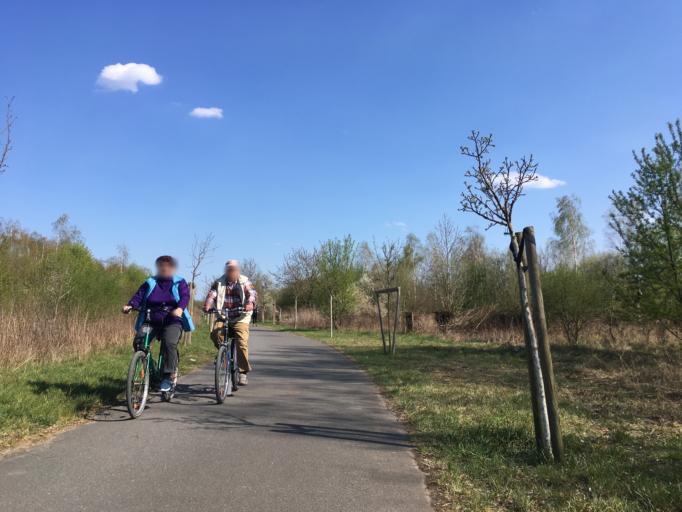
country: DE
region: Berlin
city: Wartenberg
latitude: 52.5892
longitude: 13.5008
